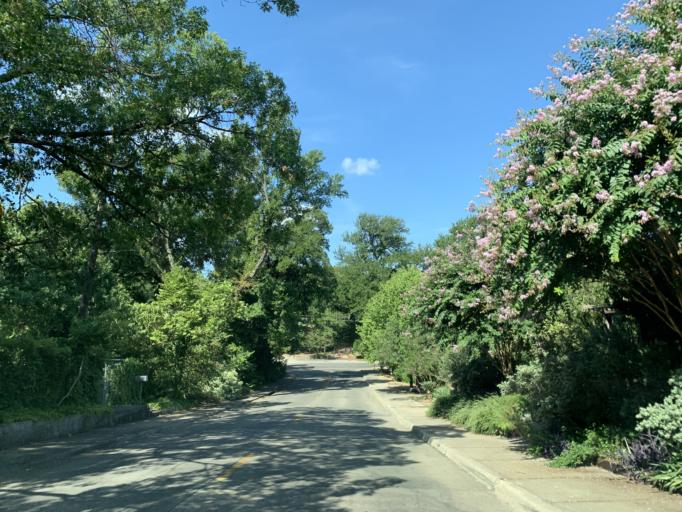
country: US
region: Texas
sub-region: Dallas County
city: Cockrell Hill
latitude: 32.7413
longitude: -96.8688
